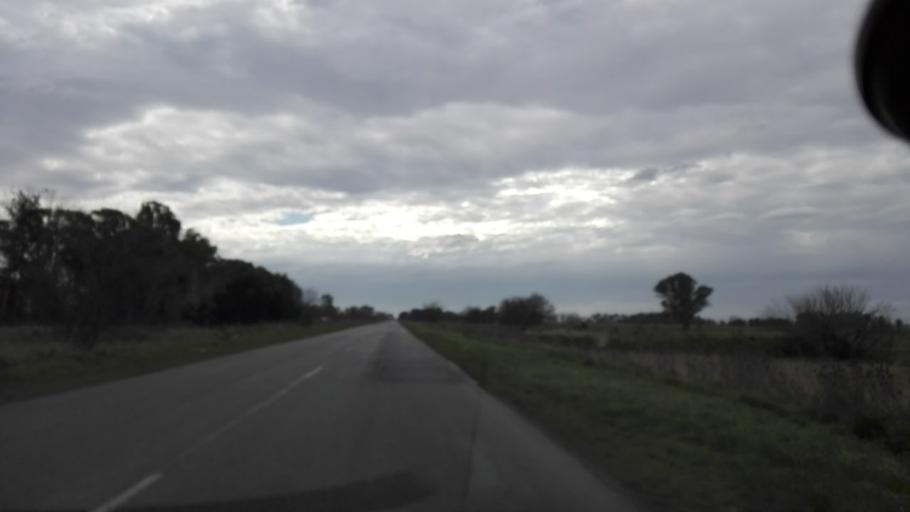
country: AR
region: Buenos Aires
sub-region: Partido de Las Flores
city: Las Flores
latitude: -36.2330
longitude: -59.0445
